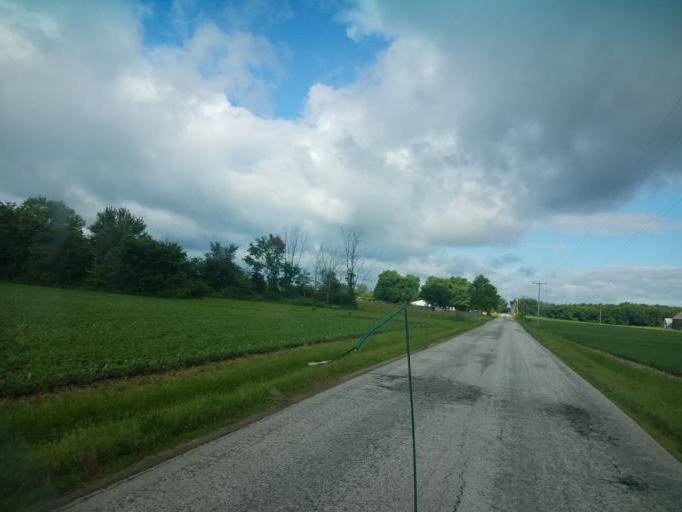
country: US
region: Ohio
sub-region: Delaware County
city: Ashley
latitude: 40.4554
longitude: -82.9948
